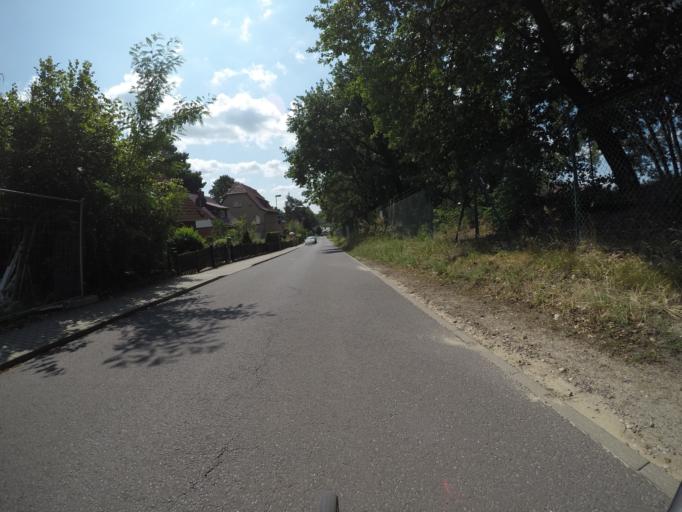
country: DE
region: Brandenburg
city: Werder
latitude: 52.4072
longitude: 12.9855
